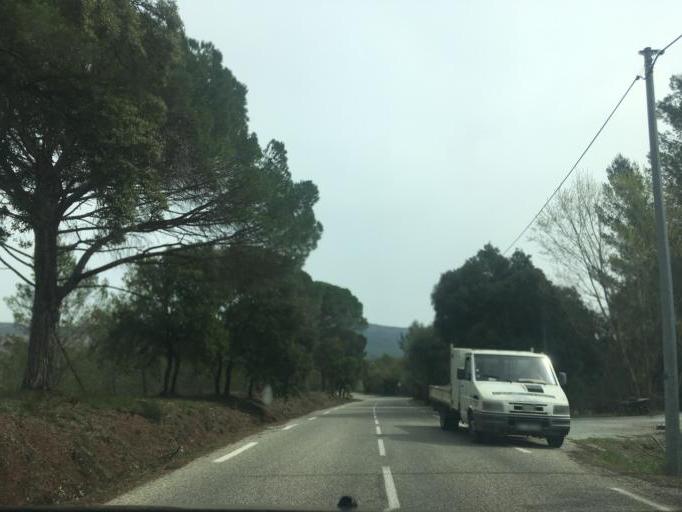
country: FR
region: Provence-Alpes-Cote d'Azur
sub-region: Departement du Var
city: Le Muy
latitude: 43.5010
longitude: 6.5818
